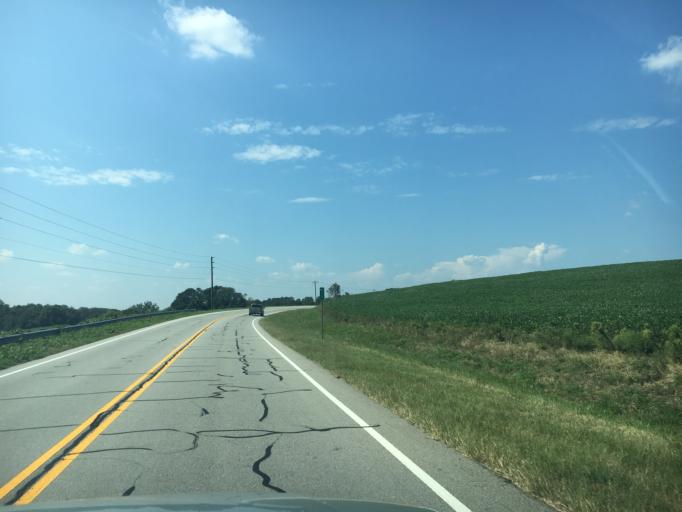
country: US
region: Georgia
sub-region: Franklin County
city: Lavonia
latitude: 34.4316
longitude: -83.0286
